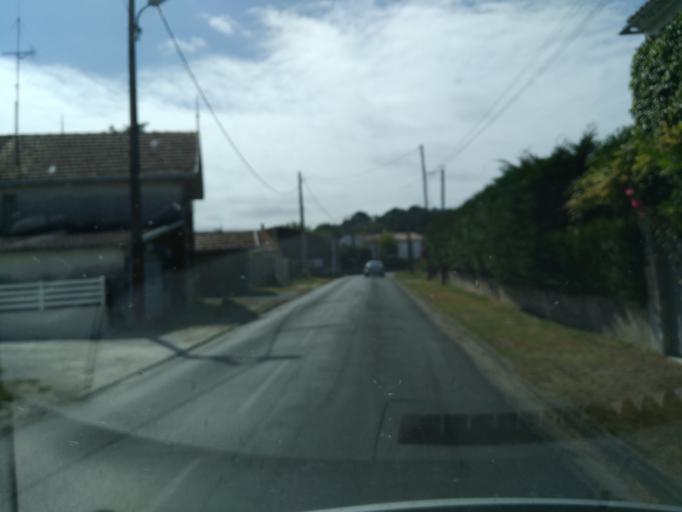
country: FR
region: Poitou-Charentes
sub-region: Departement de la Charente-Maritime
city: Saint-Palais-sur-Mer
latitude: 45.6713
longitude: -1.0848
